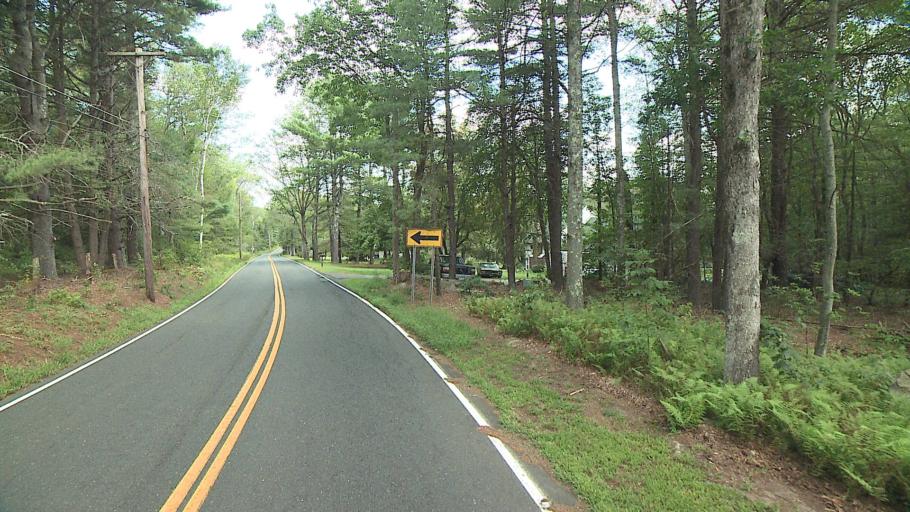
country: US
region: Connecticut
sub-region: Tolland County
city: Stafford Springs
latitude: 41.9391
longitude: -72.3385
